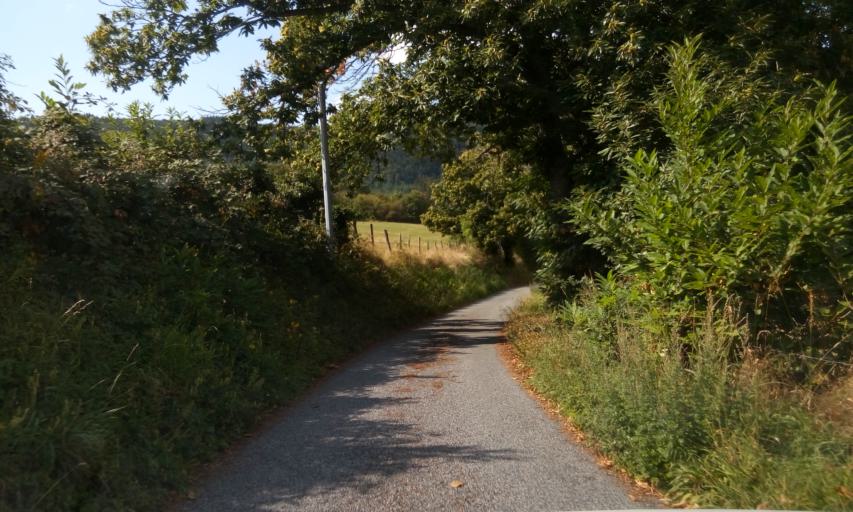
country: FR
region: Rhone-Alpes
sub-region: Departement du Rhone
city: Grandris
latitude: 46.0037
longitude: 4.4383
